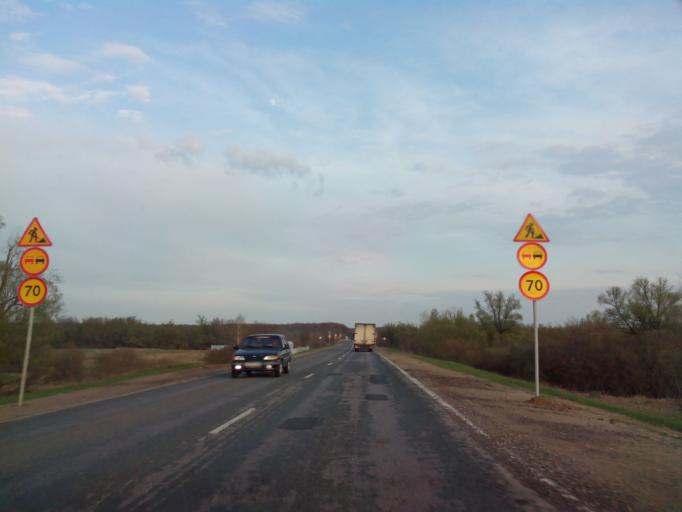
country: RU
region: Rjazan
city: Ryazhsk
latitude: 53.7169
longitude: 39.9196
